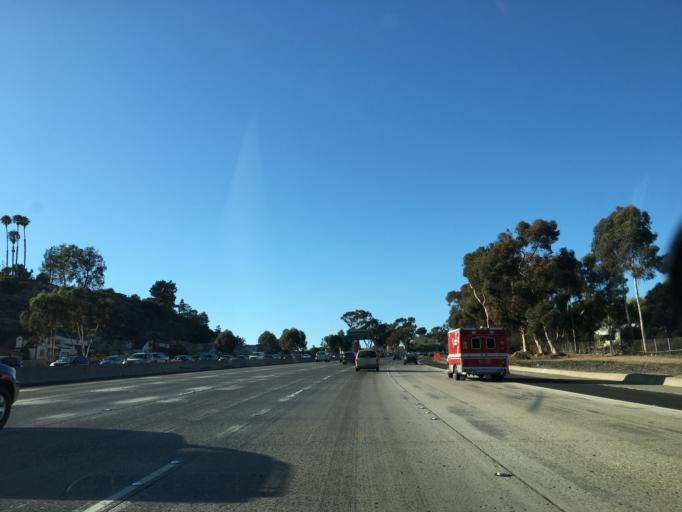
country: US
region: California
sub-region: San Diego County
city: San Diego
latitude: 32.7782
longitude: -117.1626
